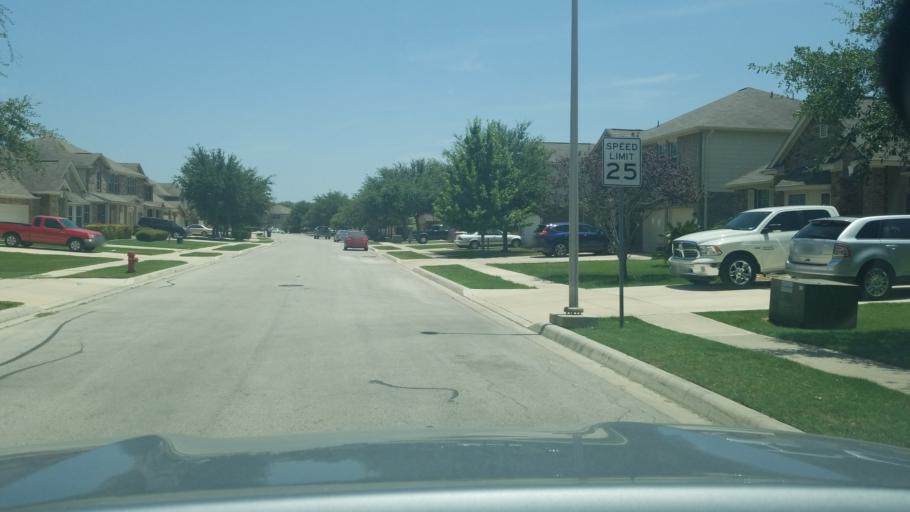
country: US
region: Texas
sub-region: Guadalupe County
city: Cibolo
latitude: 29.5756
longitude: -98.2297
